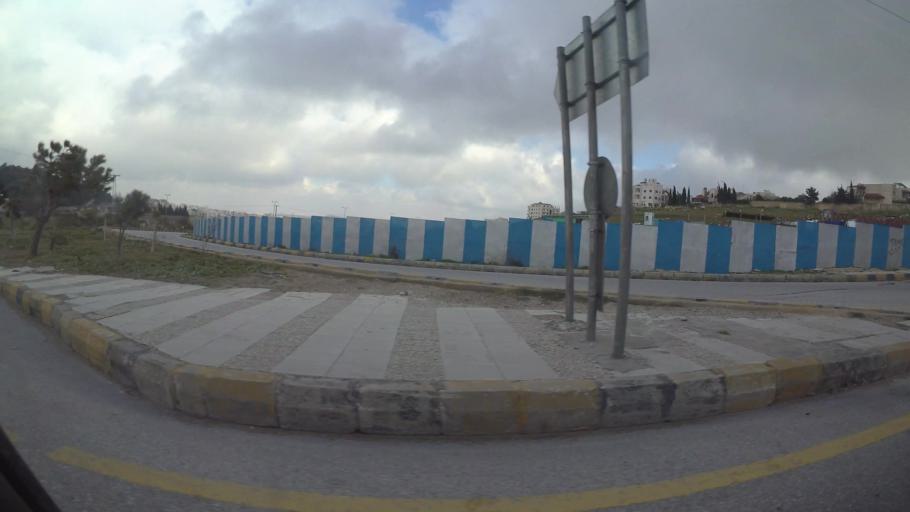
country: JO
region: Amman
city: Al Jubayhah
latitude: 32.0449
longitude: 35.8701
